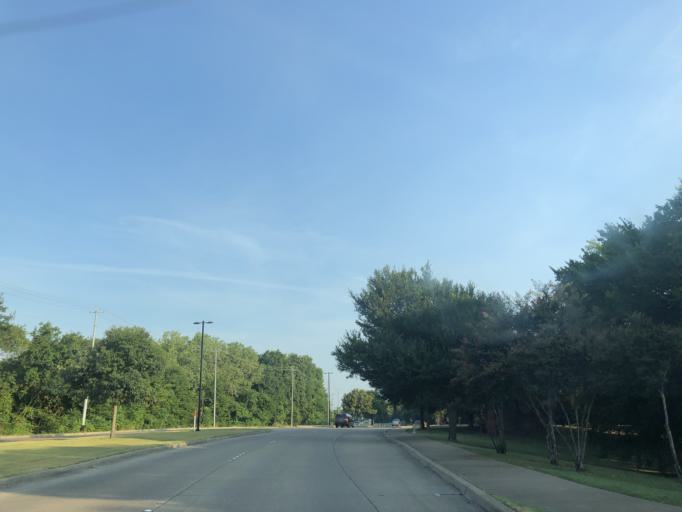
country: US
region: Texas
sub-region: Dallas County
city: Garland
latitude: 32.8620
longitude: -96.6219
